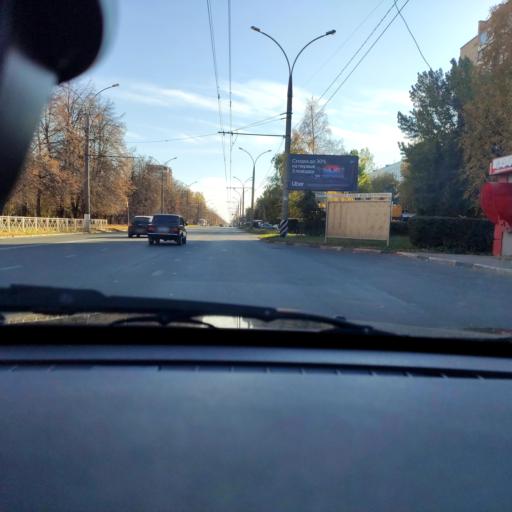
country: RU
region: Samara
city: Tol'yatti
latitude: 53.5362
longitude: 49.2779
